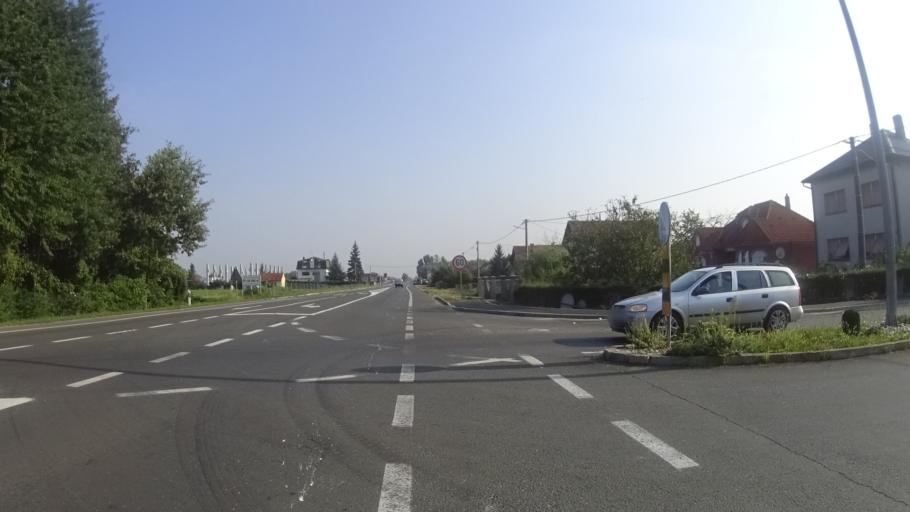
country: HR
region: Varazdinska
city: Varazdin
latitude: 46.3305
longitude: 16.3601
